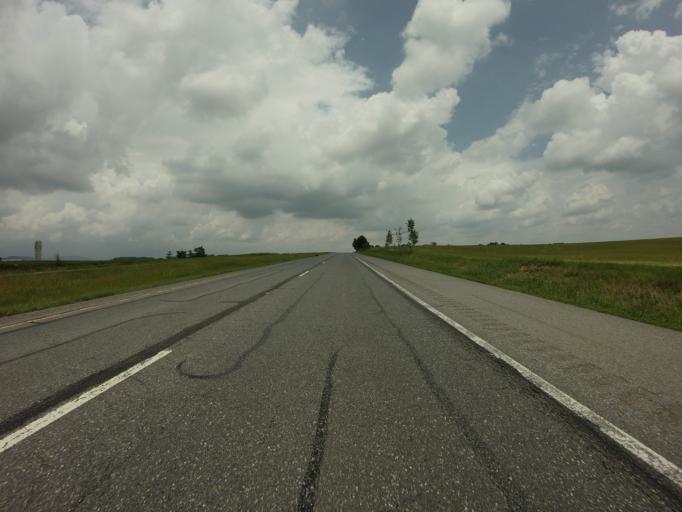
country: US
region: Maryland
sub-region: Frederick County
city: Brunswick
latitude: 39.3465
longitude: -77.6291
